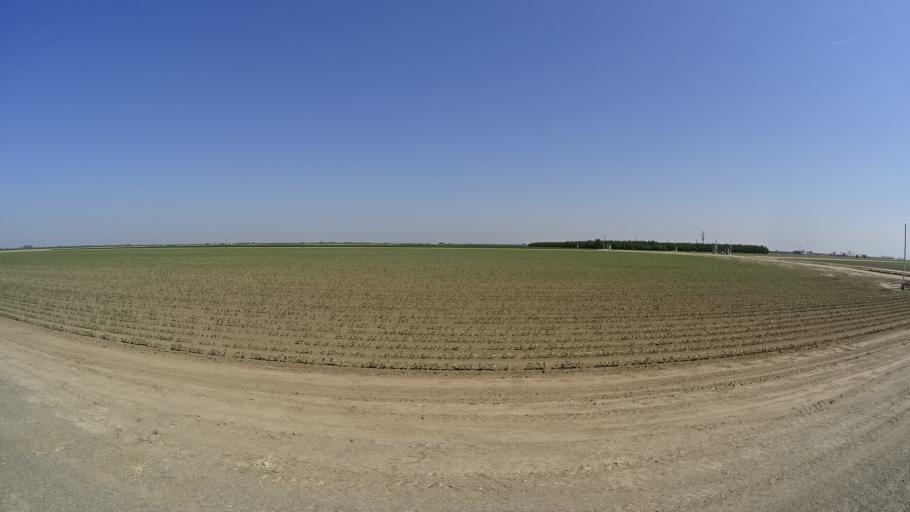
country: US
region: California
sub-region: Kings County
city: Hanford
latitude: 36.3720
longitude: -119.5599
